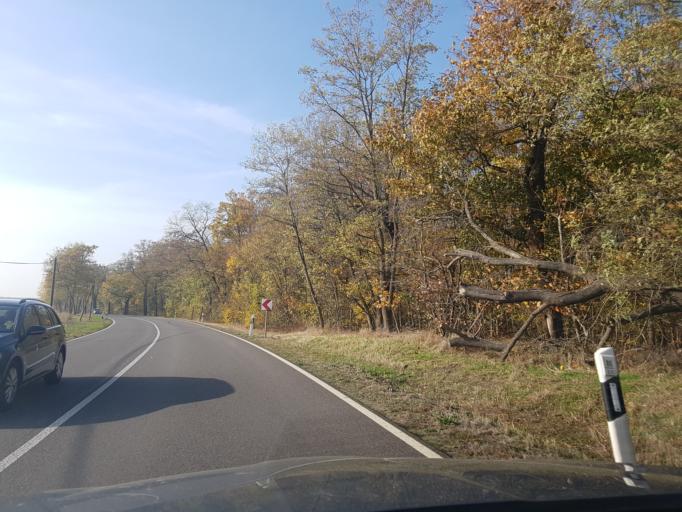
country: DE
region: Brandenburg
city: Falkenberg
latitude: 51.5448
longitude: 13.2367
